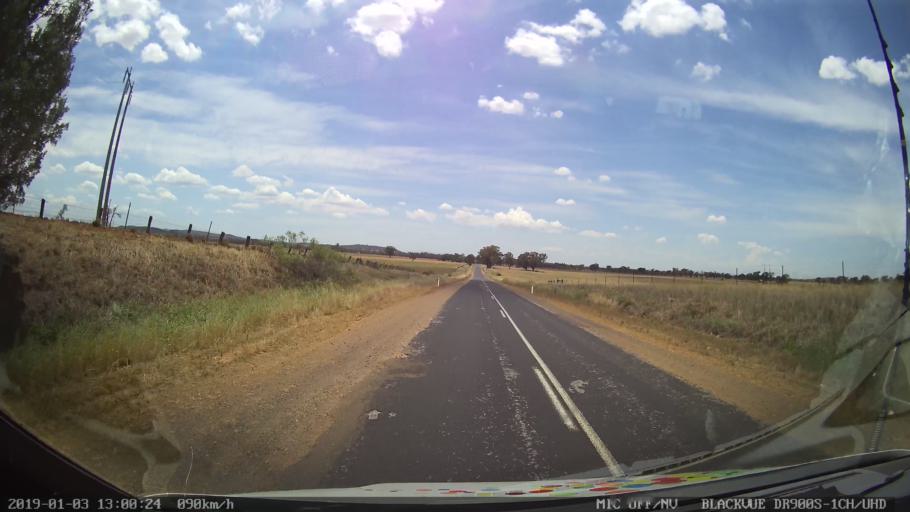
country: AU
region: New South Wales
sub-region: Cabonne
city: Canowindra
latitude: -33.6311
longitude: 148.4030
